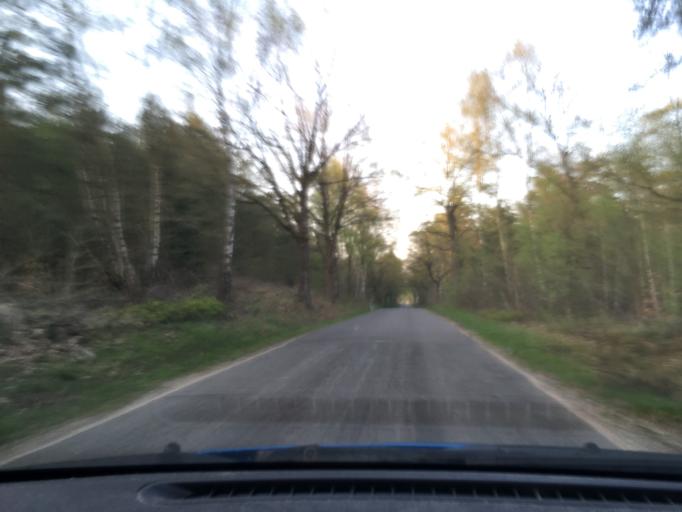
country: DE
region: Lower Saxony
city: Sudergellersen
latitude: 53.1935
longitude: 10.2776
